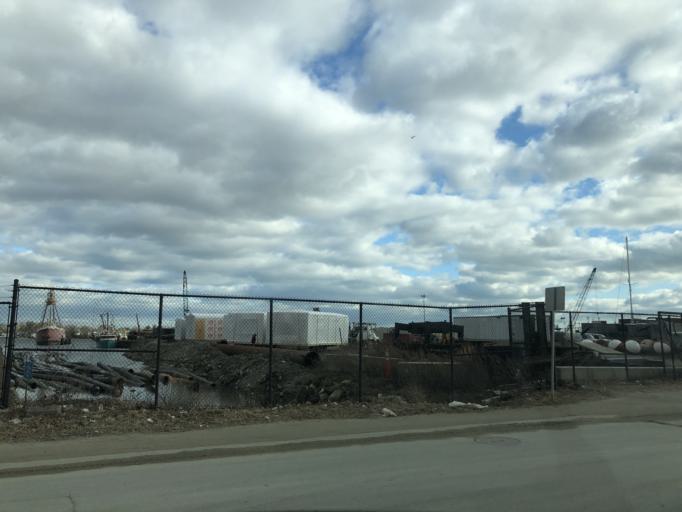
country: US
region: Massachusetts
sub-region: Bristol County
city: New Bedford
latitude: 41.6488
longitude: -70.9241
